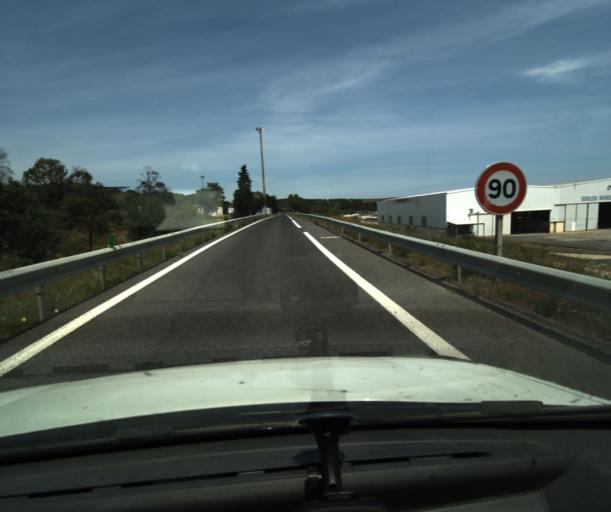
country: FR
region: Languedoc-Roussillon
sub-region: Departement des Pyrenees-Orientales
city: el Volo
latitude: 42.5269
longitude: 2.8226
